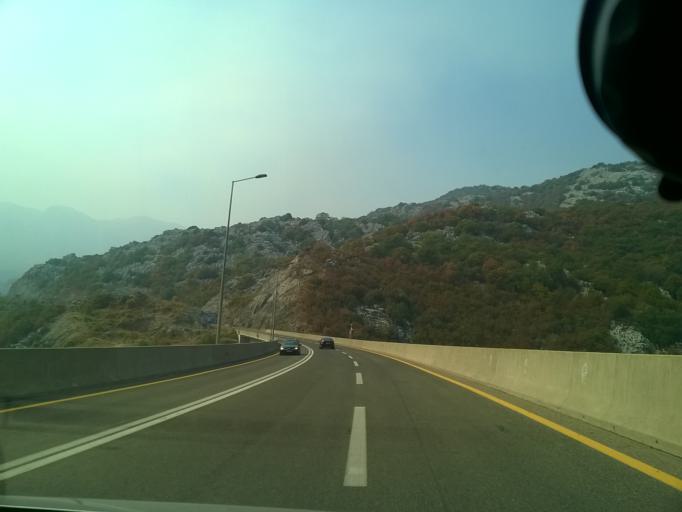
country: ME
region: Bar
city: Sutomore
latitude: 42.2260
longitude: 19.0522
